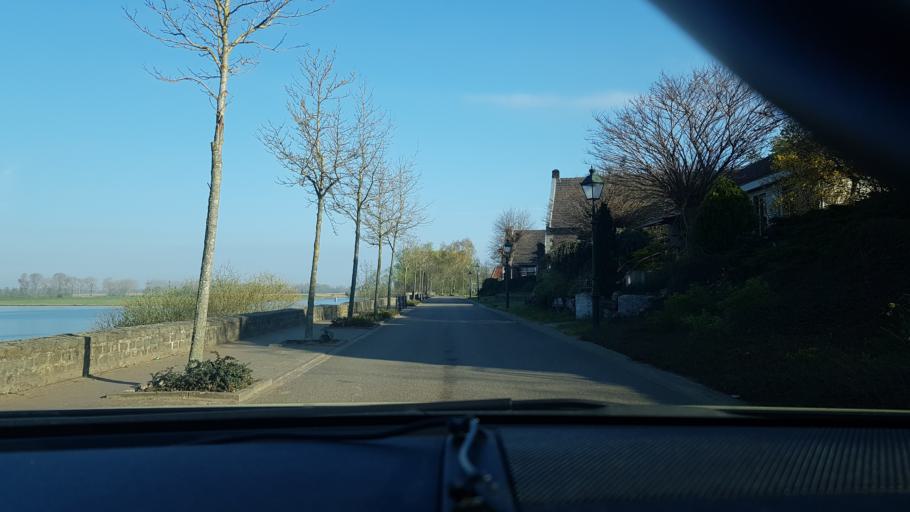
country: NL
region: Limburg
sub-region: Gemeente Roermond
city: Leeuwen
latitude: 51.2298
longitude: 6.0106
